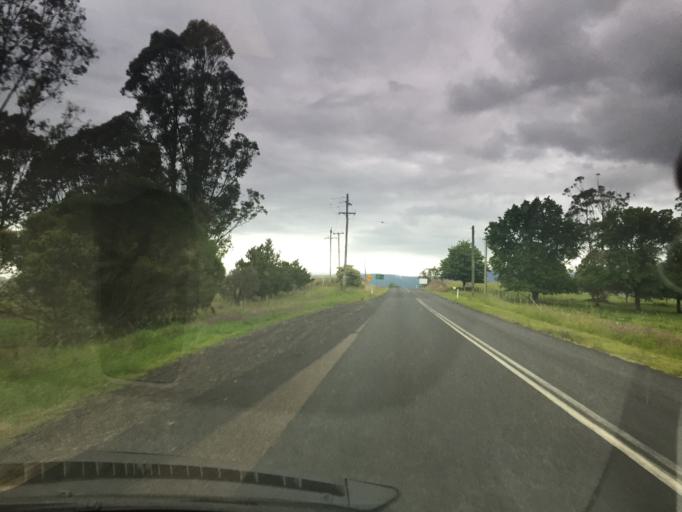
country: AU
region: New South Wales
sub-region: Bega Valley
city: Bega
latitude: -36.6446
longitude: 149.5870
